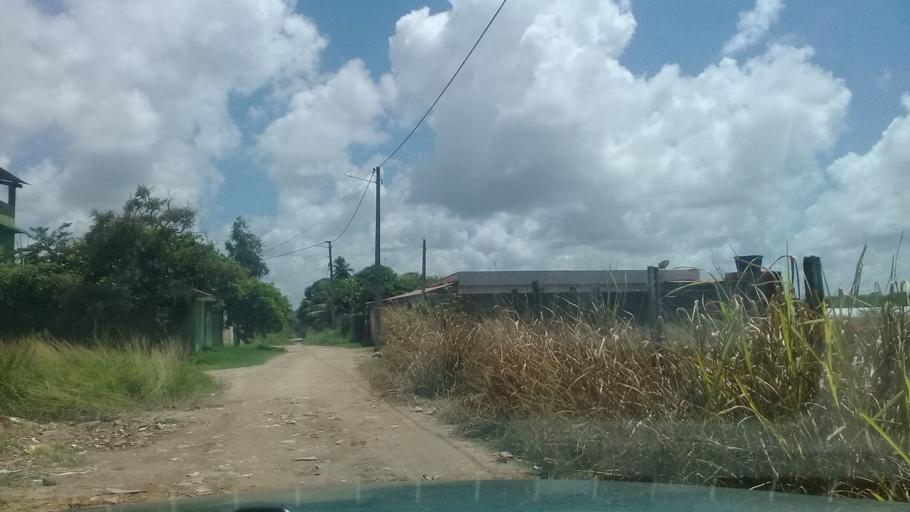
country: BR
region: Pernambuco
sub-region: Sirinhaem
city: Sirinhaem
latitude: -8.6234
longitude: -35.0639
